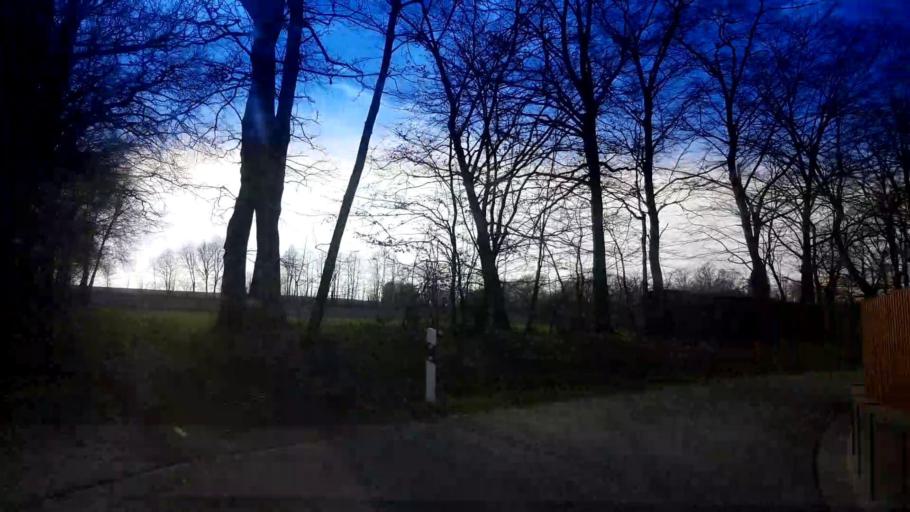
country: DE
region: Bavaria
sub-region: Upper Franconia
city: Himmelkron
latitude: 50.0274
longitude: 11.6193
